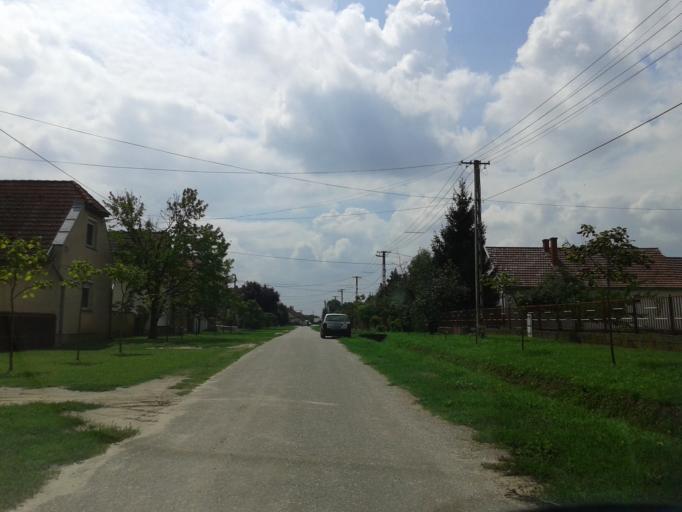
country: HU
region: Csongrad
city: Bordany
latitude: 46.3213
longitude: 19.9306
